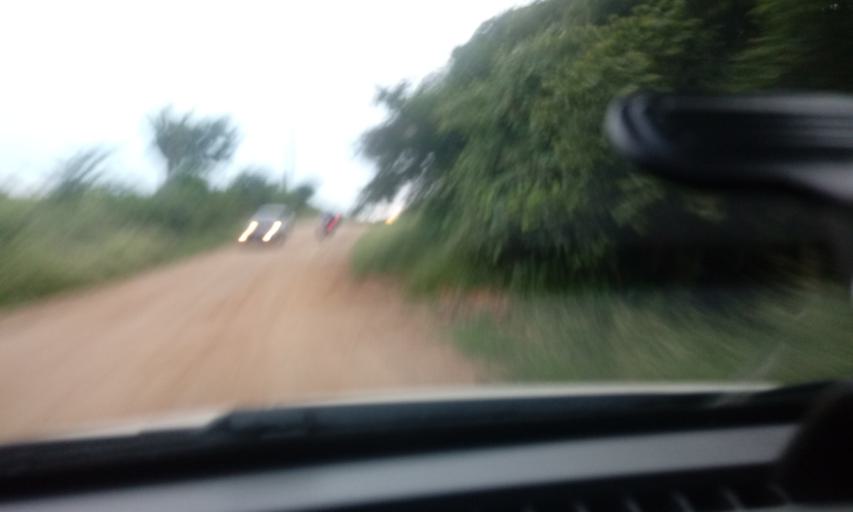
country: BR
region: Bahia
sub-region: Riacho De Santana
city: Riacho de Santana
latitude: -13.7999
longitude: -42.7389
